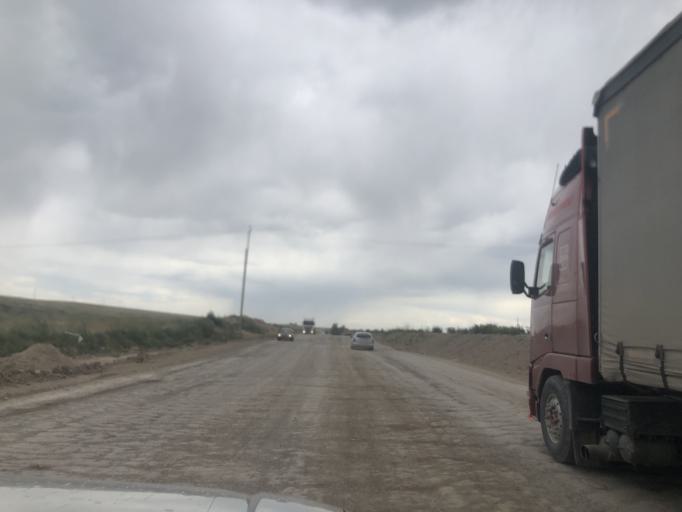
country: KG
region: Chuy
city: Bystrovka
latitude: 43.3216
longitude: 75.9856
